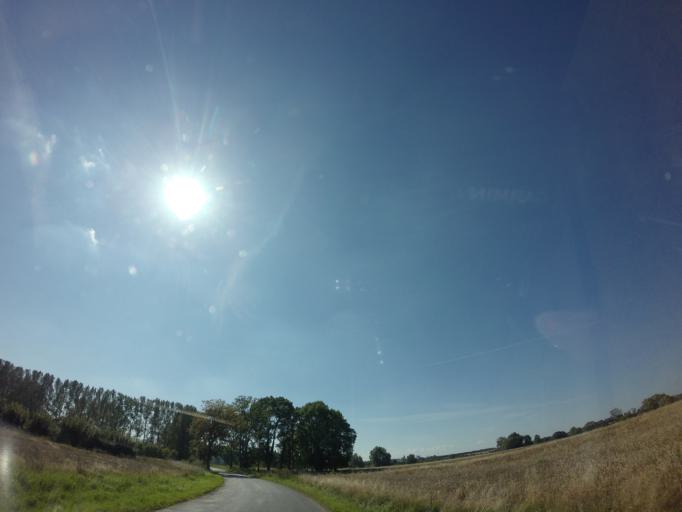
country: PL
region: West Pomeranian Voivodeship
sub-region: Powiat choszczenski
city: Choszczno
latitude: 53.1744
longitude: 15.4979
